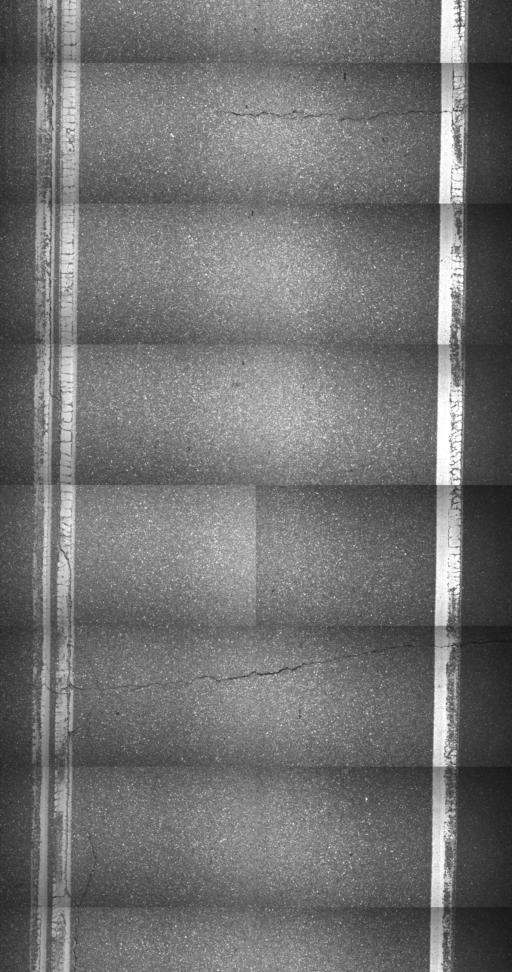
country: US
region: Vermont
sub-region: Caledonia County
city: Hardwick
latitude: 44.6219
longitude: -72.2111
